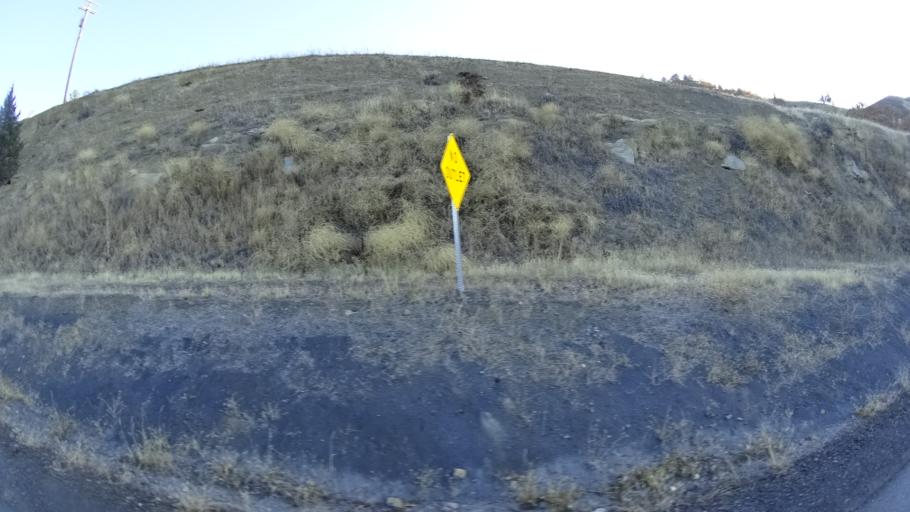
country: US
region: Oregon
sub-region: Jackson County
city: Ashland
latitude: 41.9931
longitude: -122.6087
